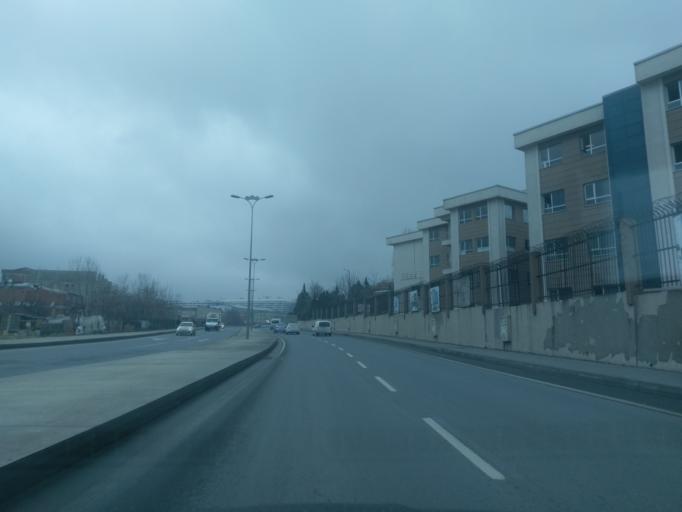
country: TR
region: Istanbul
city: Basaksehir
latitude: 41.0742
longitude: 28.7936
